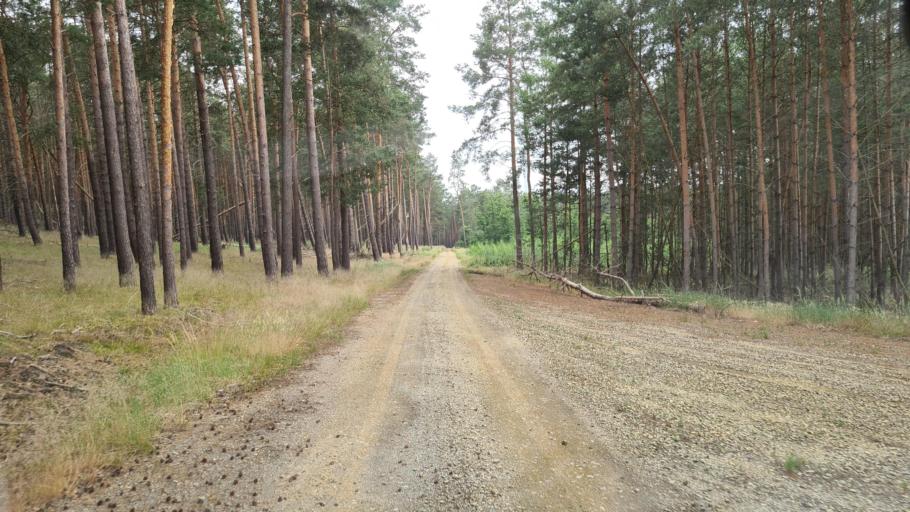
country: DE
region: Brandenburg
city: Schlieben
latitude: 51.6637
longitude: 13.3545
